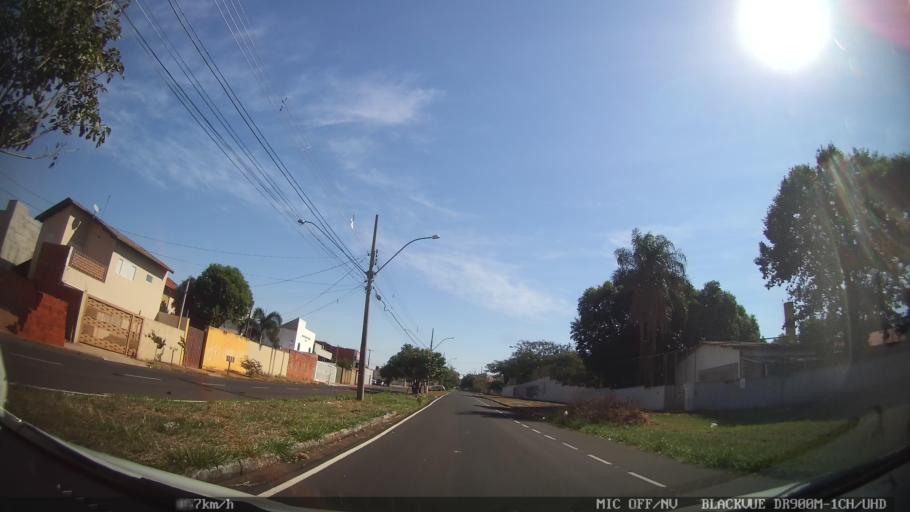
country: BR
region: Sao Paulo
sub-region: Sao Jose Do Rio Preto
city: Sao Jose do Rio Preto
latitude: -20.7810
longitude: -49.4186
